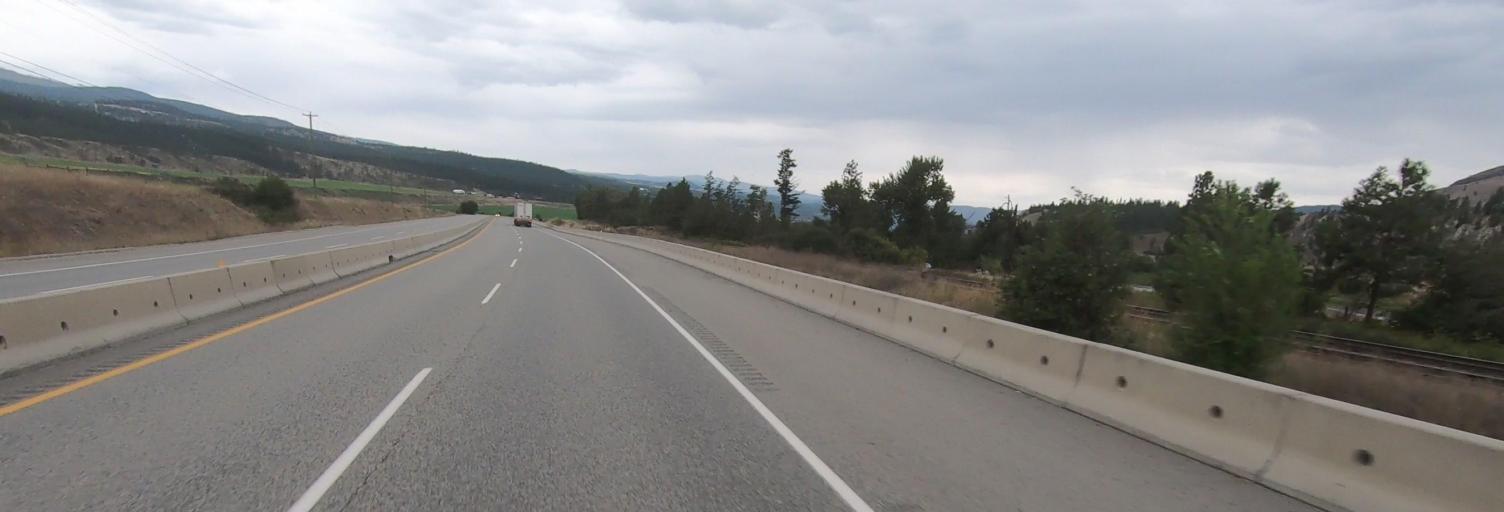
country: CA
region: British Columbia
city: Chase
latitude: 50.7097
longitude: -119.7907
